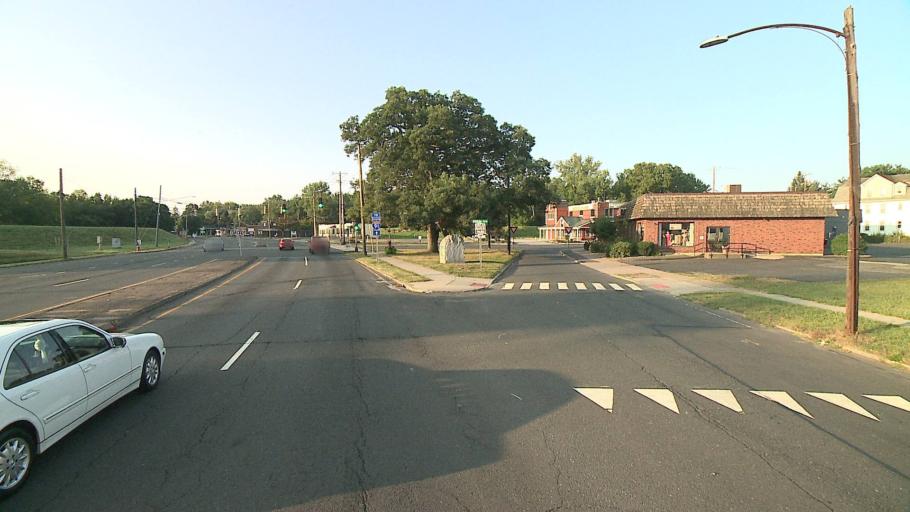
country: US
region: Connecticut
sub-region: Hartford County
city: Hartford
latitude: 41.7644
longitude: -72.6466
